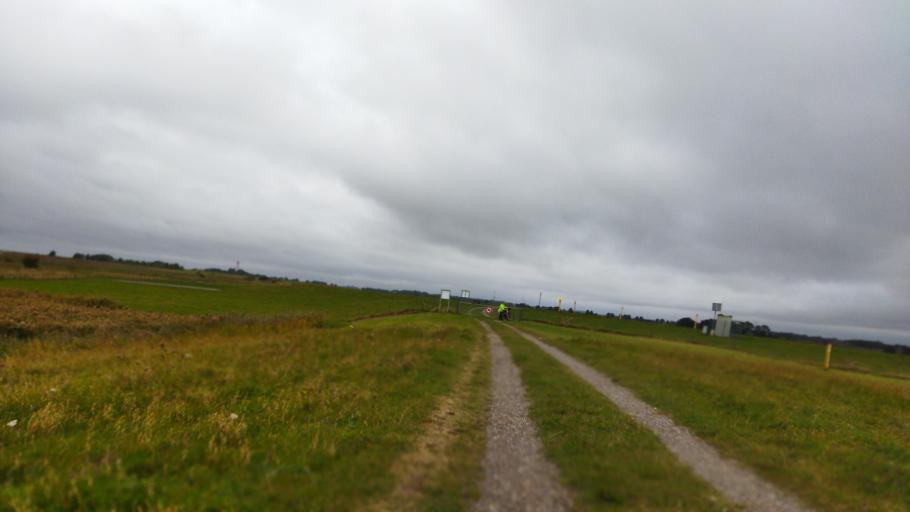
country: NL
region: Groningen
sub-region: Gemeente Delfzijl
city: Delfzijl
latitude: 53.3781
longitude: 7.0144
